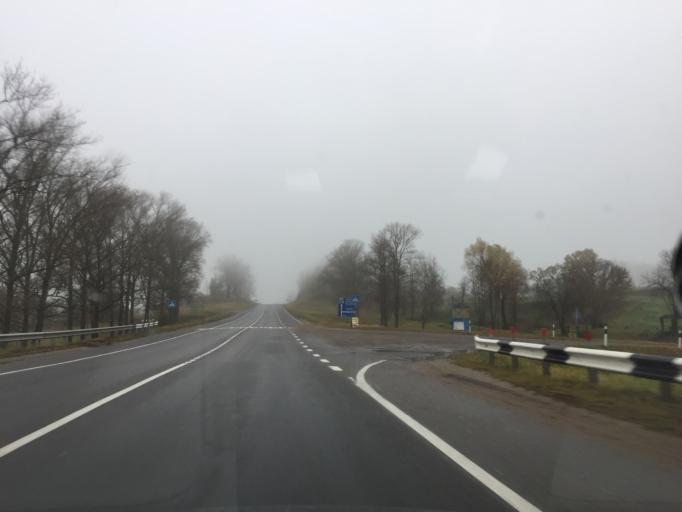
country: BY
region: Mogilev
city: Shklow
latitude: 54.1712
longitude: 30.4551
